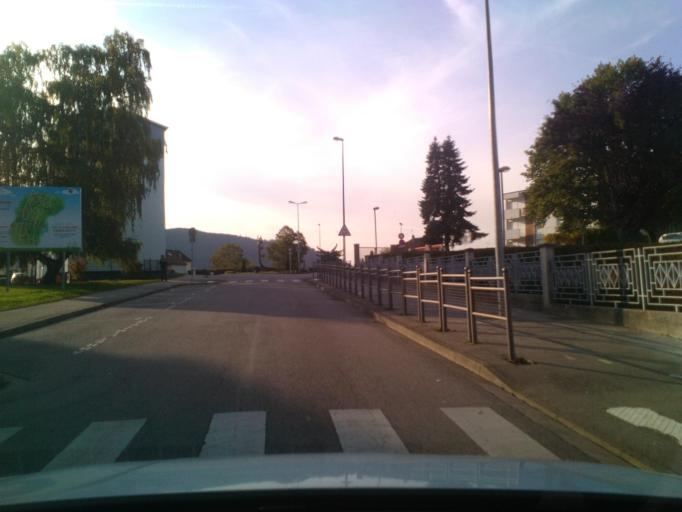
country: FR
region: Lorraine
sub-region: Departement des Vosges
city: Saint-Die-des-Vosges
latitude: 48.2968
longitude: 6.9478
